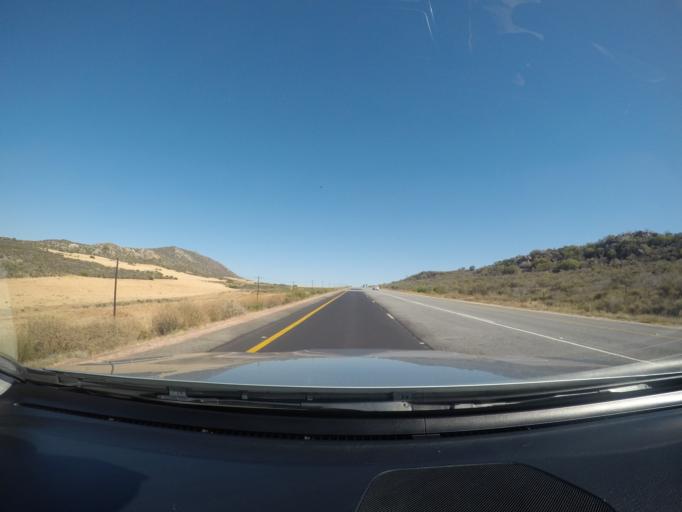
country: ZA
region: Western Cape
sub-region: West Coast District Municipality
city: Clanwilliam
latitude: -32.2957
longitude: 18.9003
